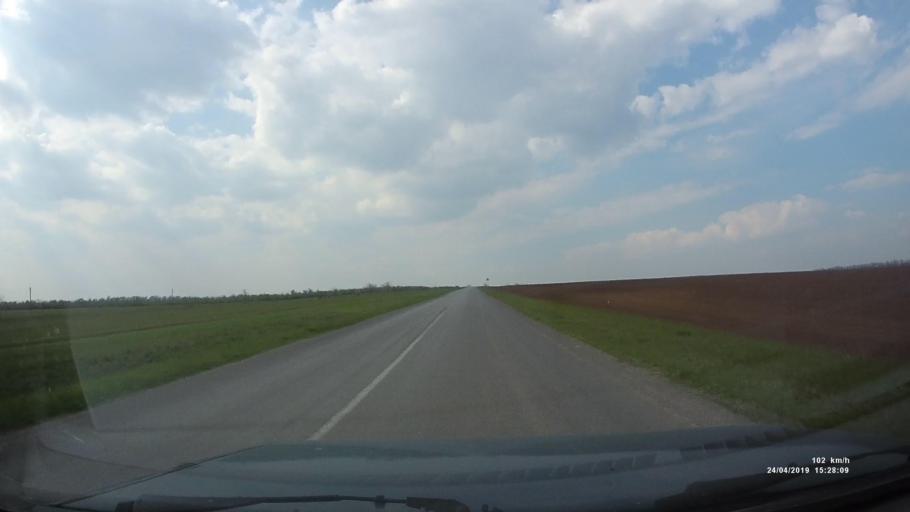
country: RU
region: Rostov
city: Remontnoye
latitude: 46.5750
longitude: 43.0204
